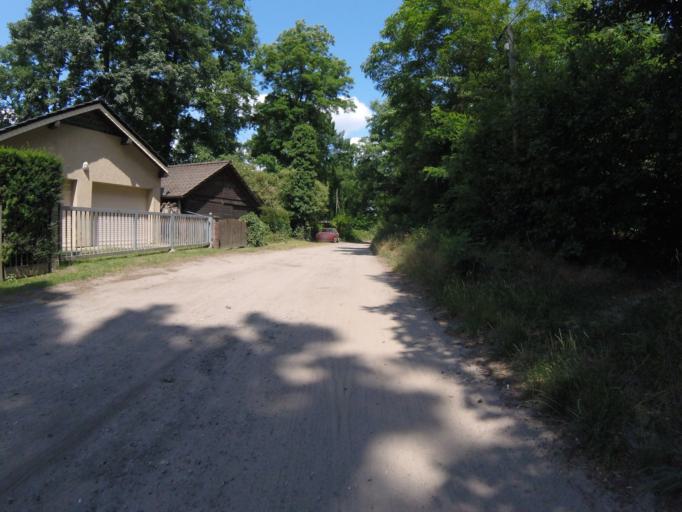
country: DE
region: Brandenburg
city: Konigs Wusterhausen
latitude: 52.2836
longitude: 13.6578
